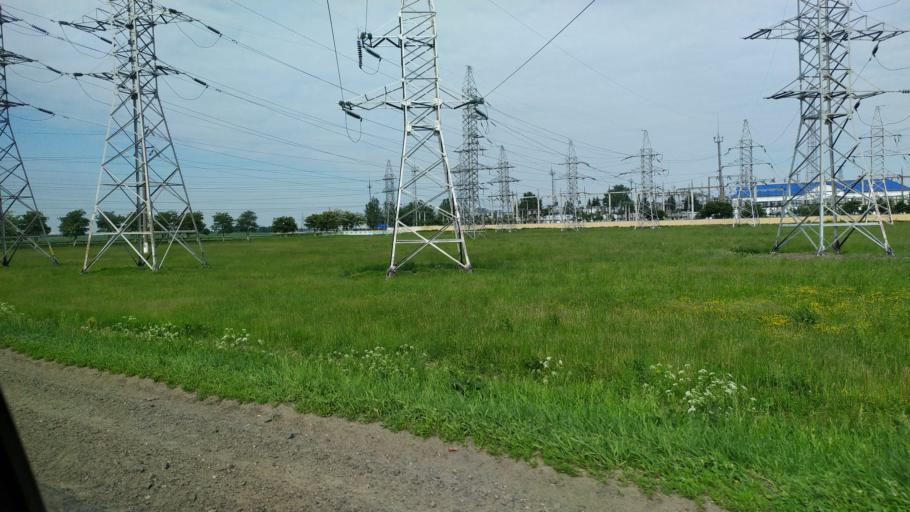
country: BY
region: Gomel
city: Gomel
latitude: 52.4567
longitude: 30.9019
